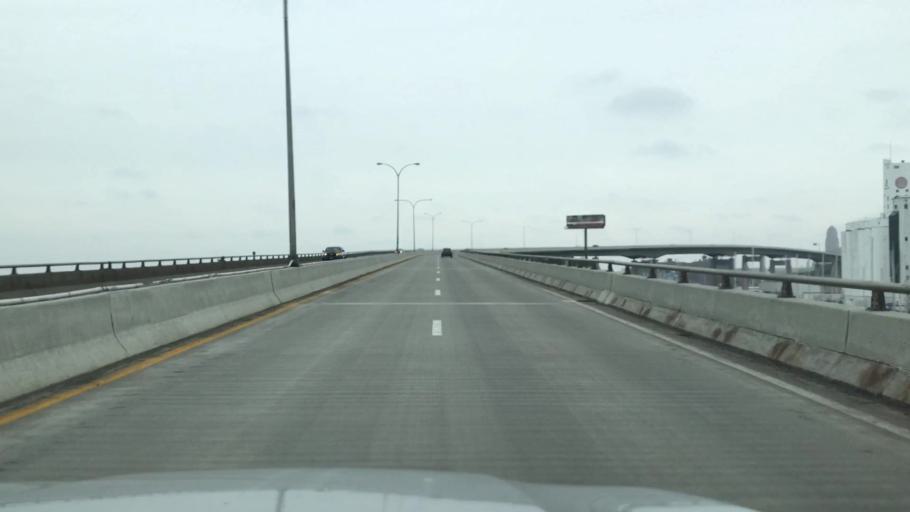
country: US
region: New York
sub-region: Erie County
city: Buffalo
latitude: 42.8678
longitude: -78.8774
